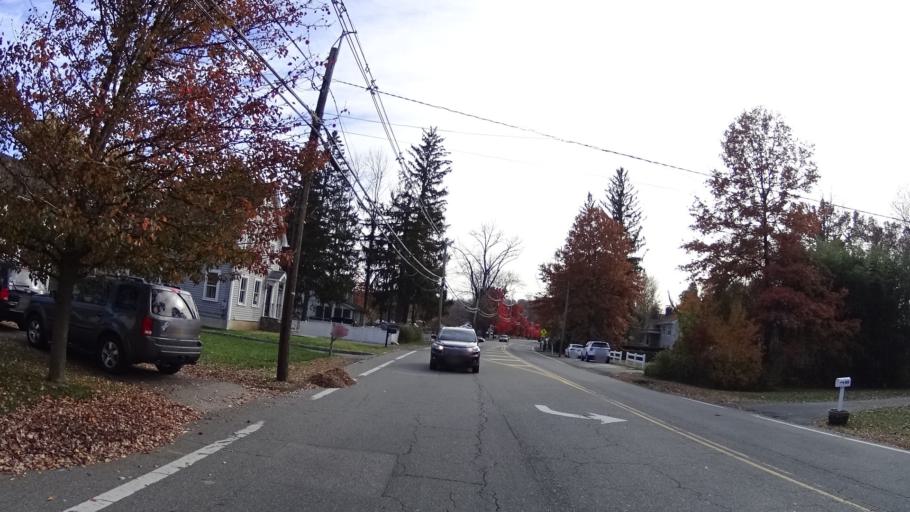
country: US
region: New Jersey
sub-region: Morris County
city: Morristown
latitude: 40.7783
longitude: -74.4670
